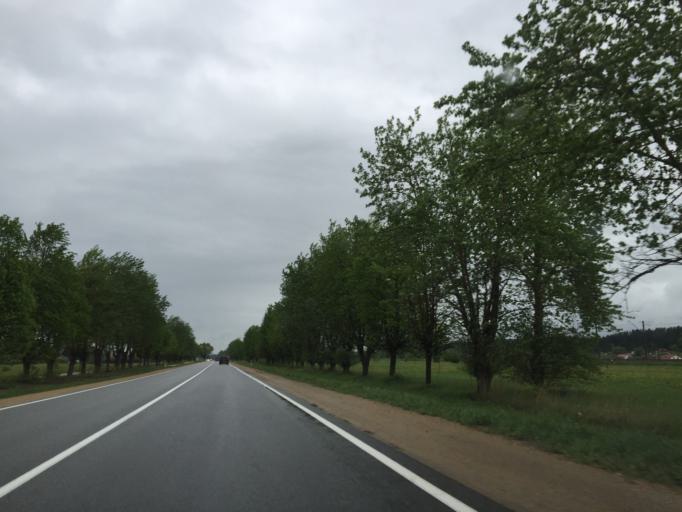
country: LV
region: Ogre
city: Ogre
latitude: 56.7891
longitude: 24.6396
